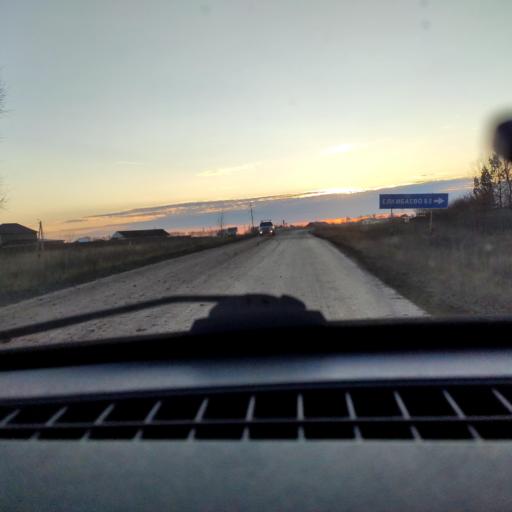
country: RU
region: Bashkortostan
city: Ufa
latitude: 54.7058
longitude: 56.1043
